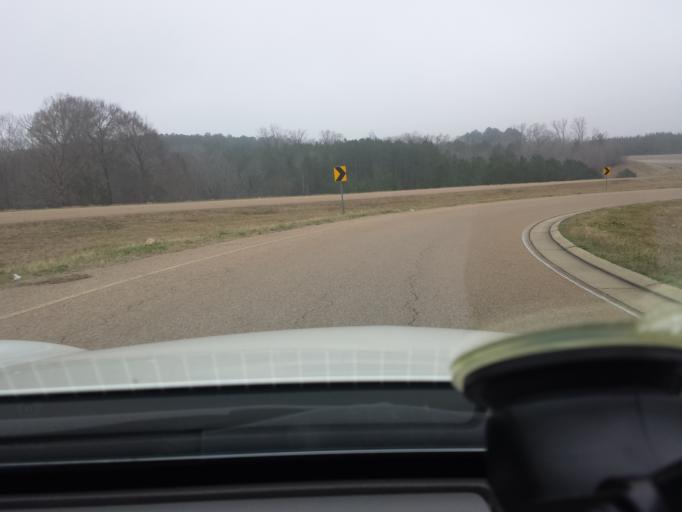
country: US
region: Mississippi
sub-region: Winston County
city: Louisville
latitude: 33.1567
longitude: -89.0891
